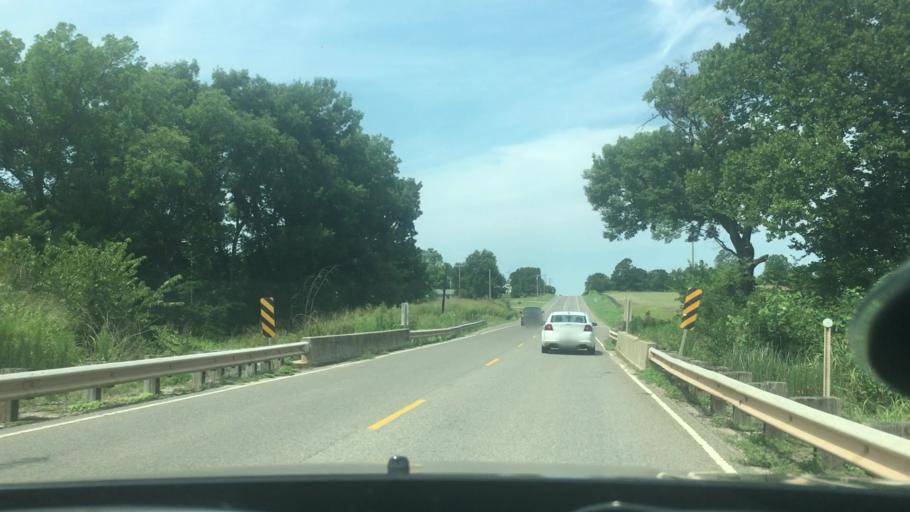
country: US
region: Oklahoma
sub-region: Pottawatomie County
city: Shawnee
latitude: 35.3332
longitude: -96.8444
